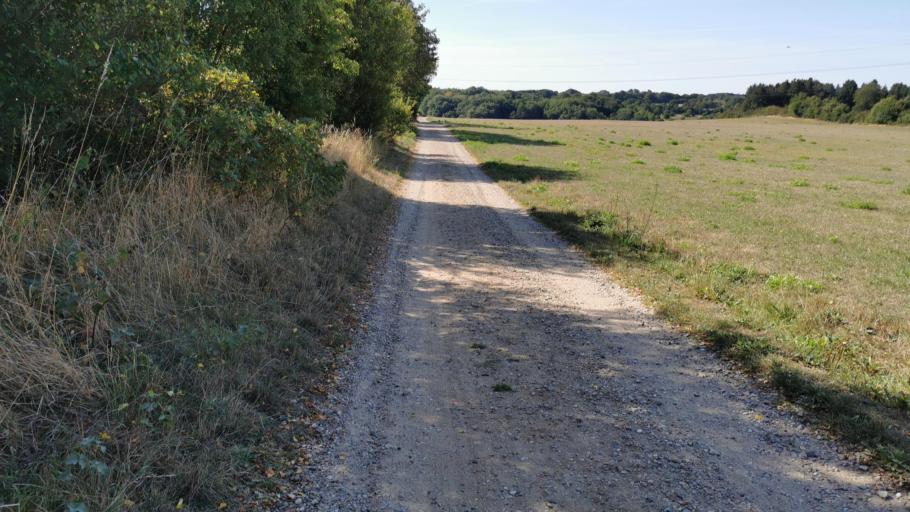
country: DK
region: South Denmark
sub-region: Kolding Kommune
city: Kolding
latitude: 55.4811
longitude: 9.4349
